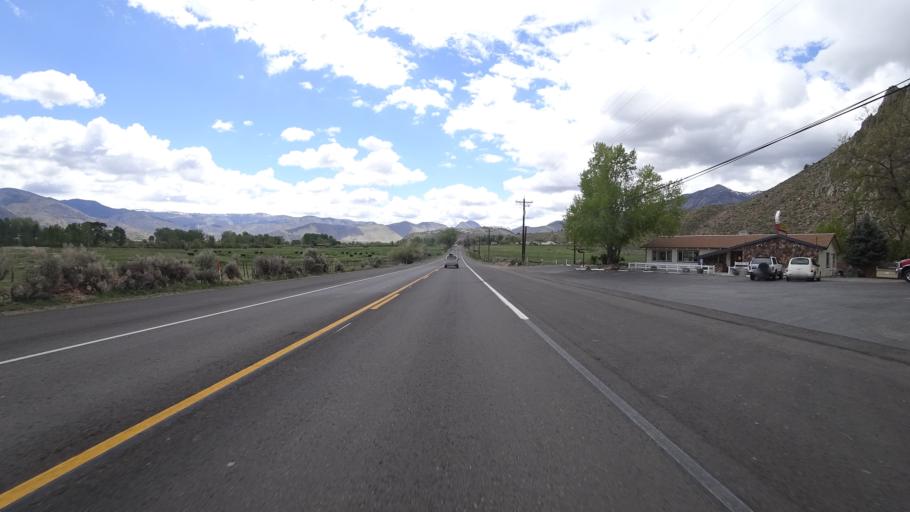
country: US
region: Nevada
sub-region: Lyon County
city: Smith Valley
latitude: 38.5521
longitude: -119.5022
